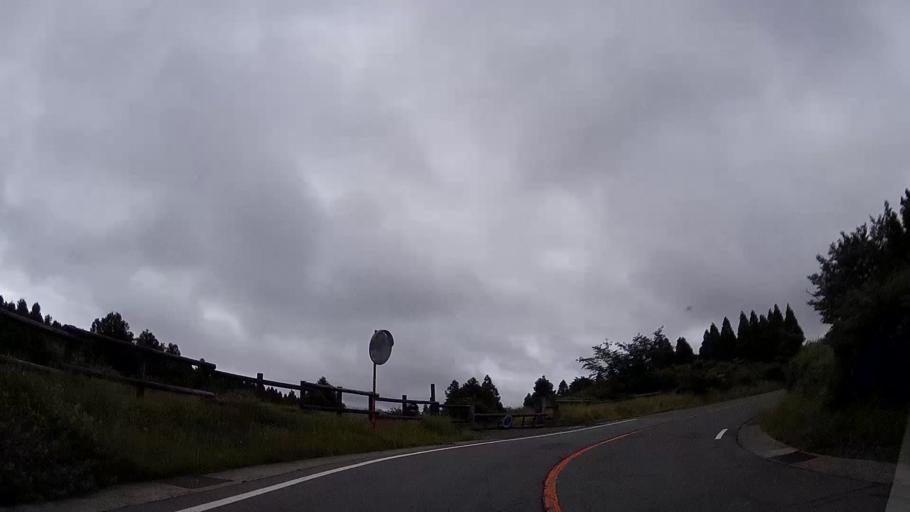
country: JP
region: Kumamoto
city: Aso
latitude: 32.8882
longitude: 131.0551
